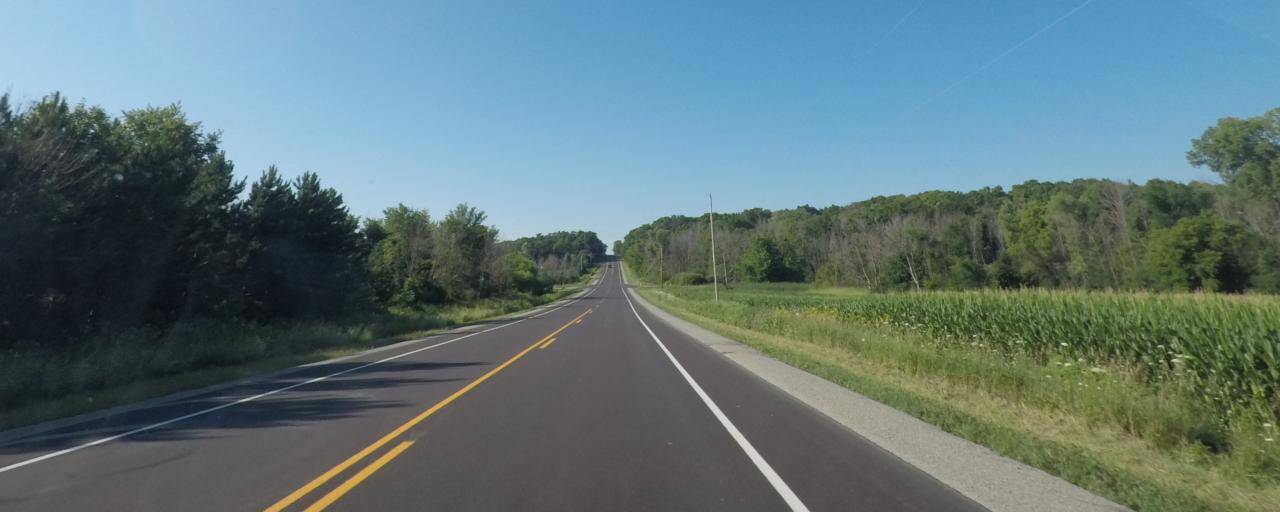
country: US
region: Wisconsin
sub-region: Jefferson County
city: Palmyra
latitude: 42.9168
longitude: -88.5866
